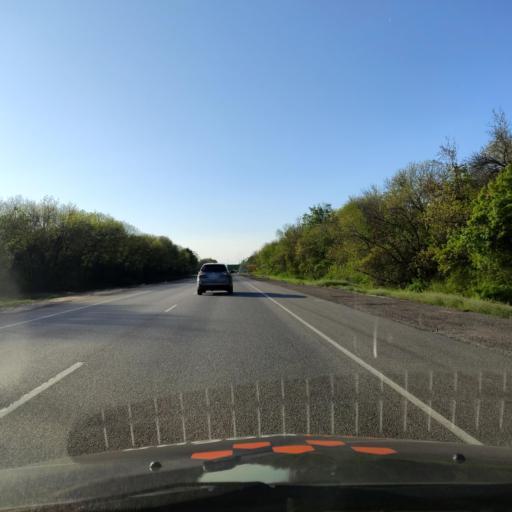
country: RU
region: Lipetsk
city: Yelets
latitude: 52.5507
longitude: 38.7096
